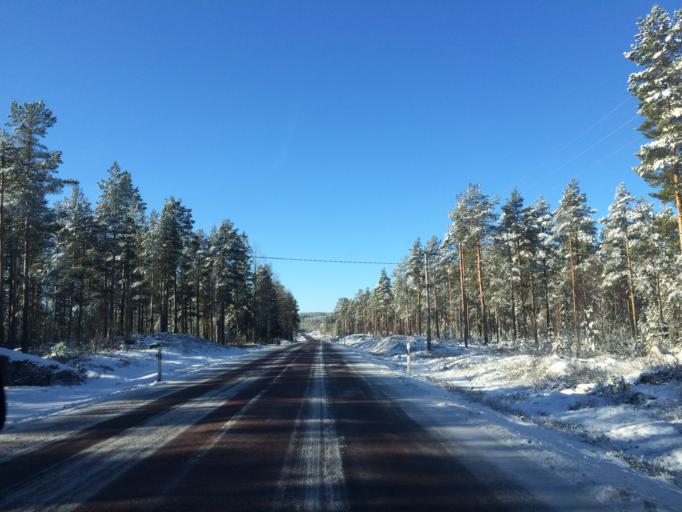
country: SE
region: Dalarna
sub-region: Vansbro Kommun
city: Vansbro
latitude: 60.8427
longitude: 14.1507
